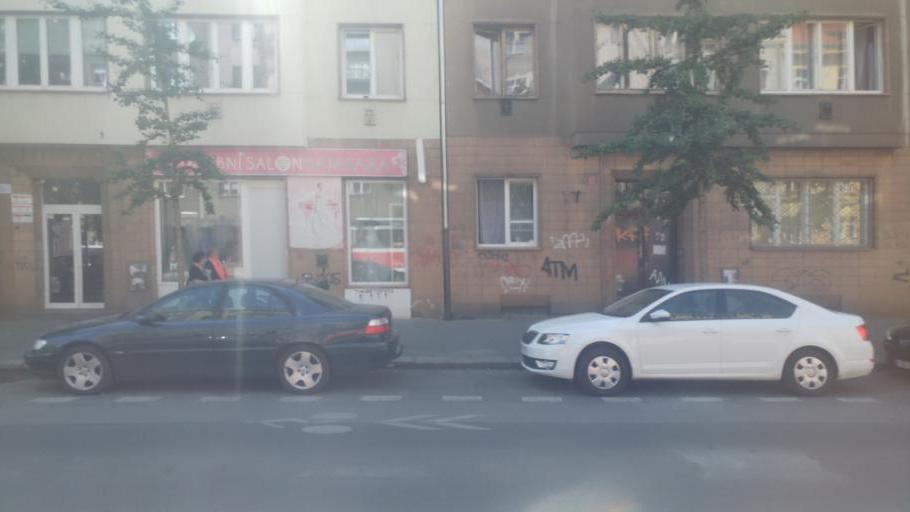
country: CZ
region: Praha
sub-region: Praha 8
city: Karlin
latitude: 50.0660
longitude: 14.4504
